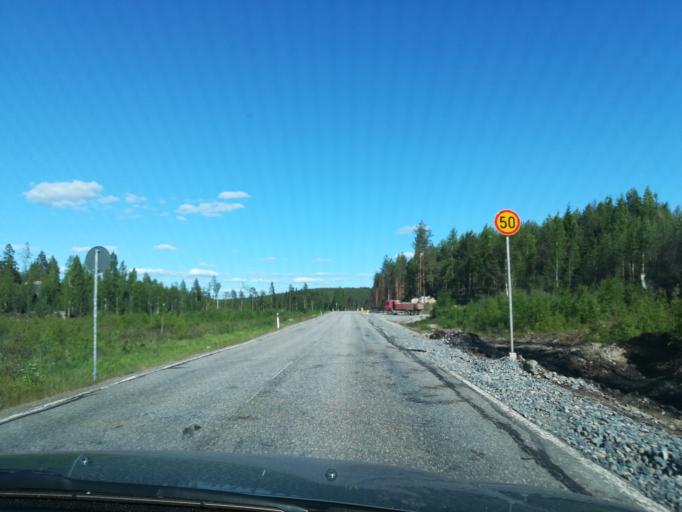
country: FI
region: Southern Savonia
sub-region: Mikkeli
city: Puumala
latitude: 61.4646
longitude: 28.3800
